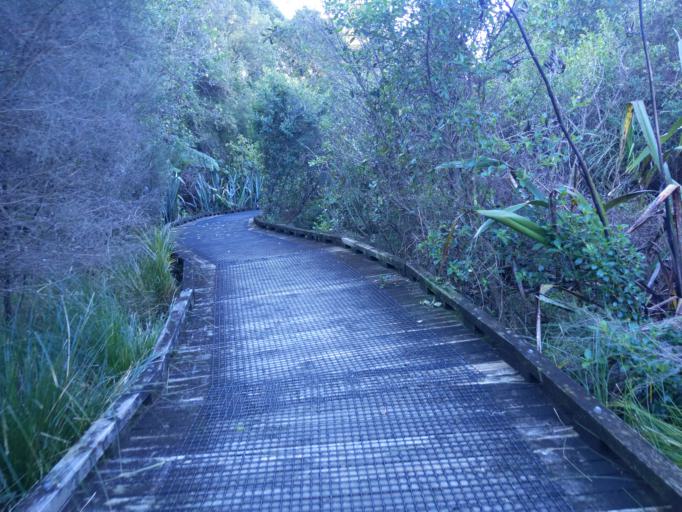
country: NZ
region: Waikato
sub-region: Hamilton City
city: Hamilton
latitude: -37.7407
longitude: 175.2763
